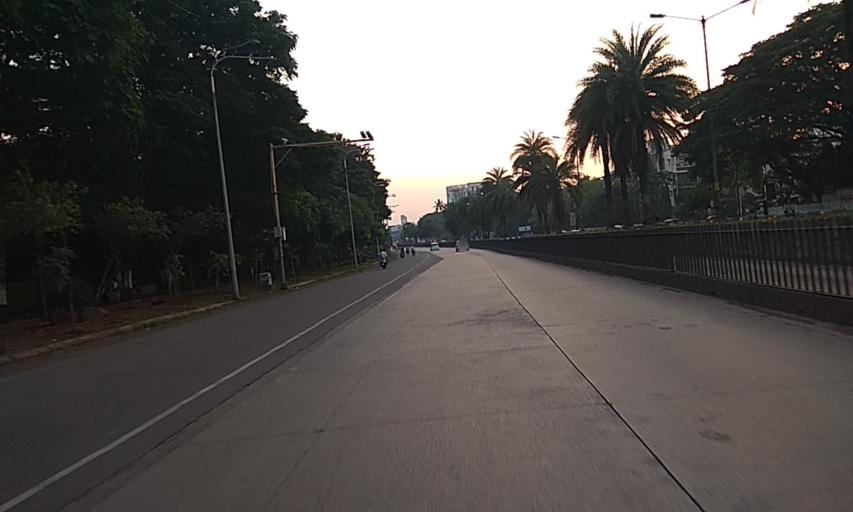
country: IN
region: Maharashtra
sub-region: Pune Division
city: Khadki
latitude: 18.5508
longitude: 73.8947
